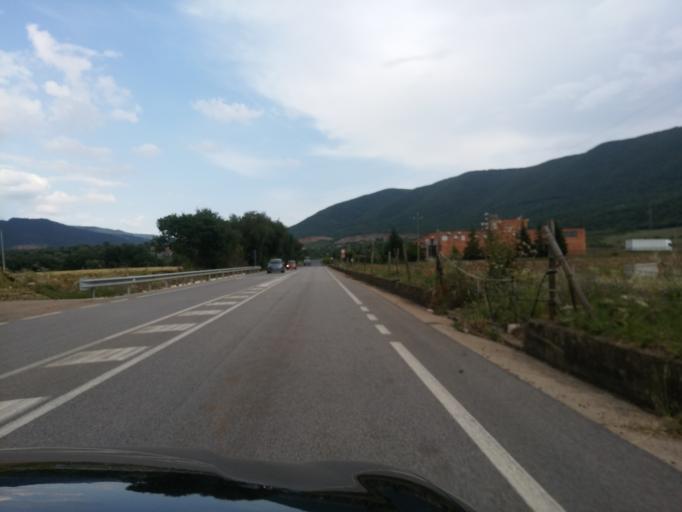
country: IT
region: Apulia
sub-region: Provincia di Foggia
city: Rignano Garganico
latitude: 41.7153
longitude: 15.5386
